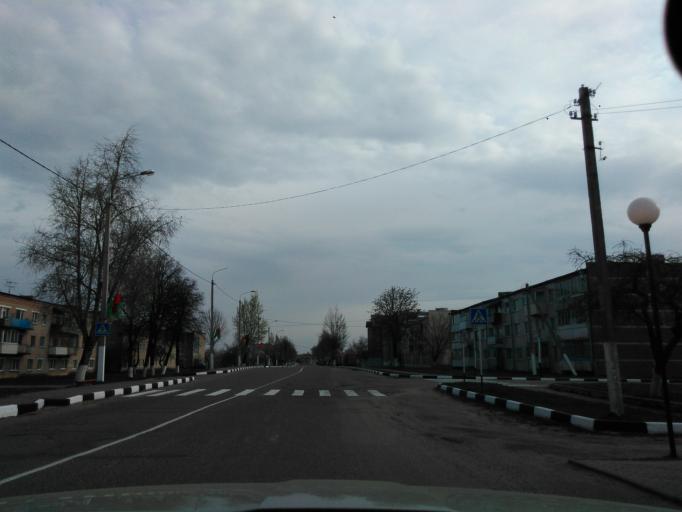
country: BY
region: Vitebsk
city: Chashniki
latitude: 54.8525
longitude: 29.1569
